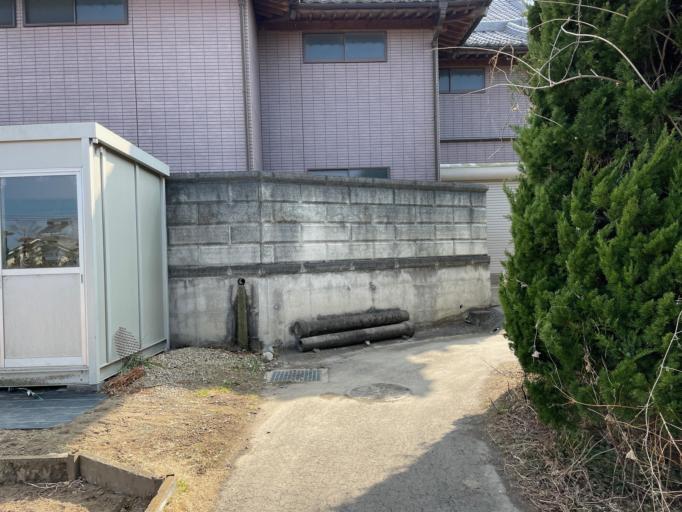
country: JP
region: Saitama
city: Yorii
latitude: 36.1256
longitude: 139.2323
